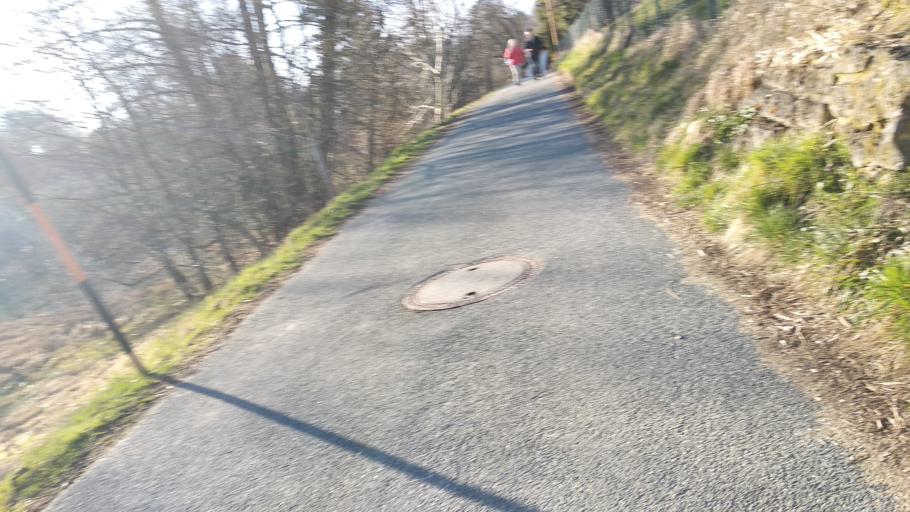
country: DE
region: Bavaria
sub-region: Upper Bavaria
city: Ebersberg
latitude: 48.0826
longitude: 11.9614
